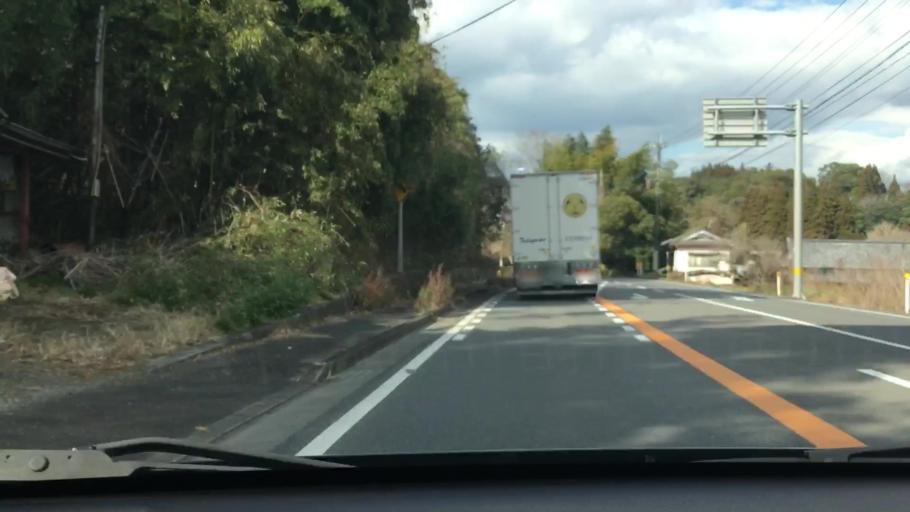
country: JP
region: Oita
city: Usuki
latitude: 33.0295
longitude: 131.6940
